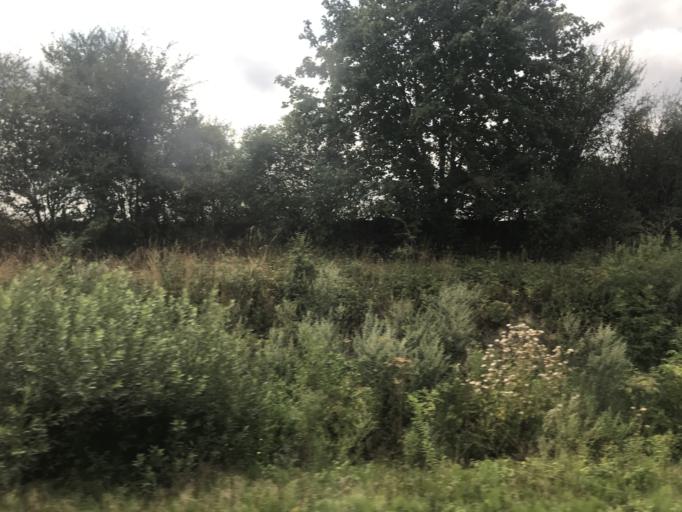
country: PL
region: Greater Poland Voivodeship
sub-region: Powiat gnieznienski
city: Lubowo
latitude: 52.5017
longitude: 17.4495
